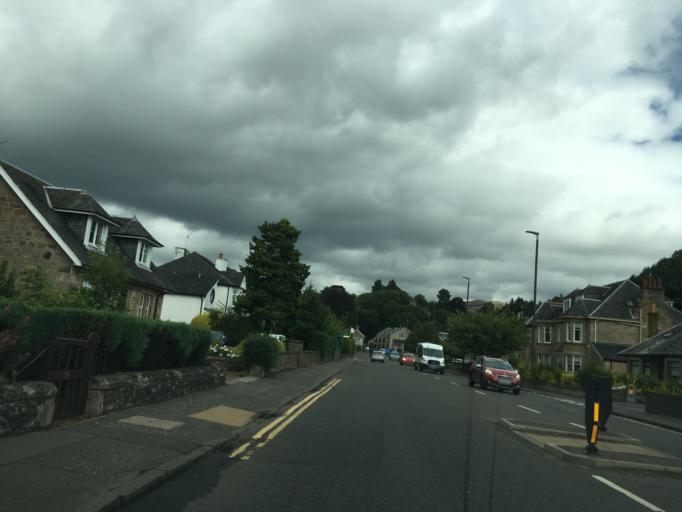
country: GB
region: Scotland
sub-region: Stirling
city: Stirling
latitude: 56.1367
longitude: -3.9258
